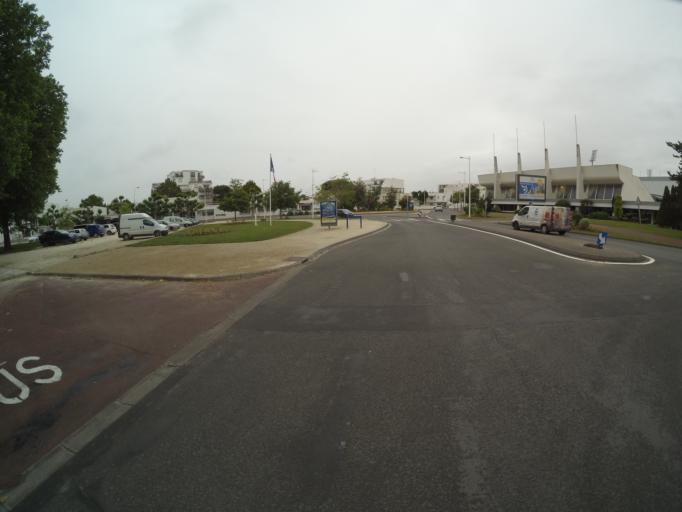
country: FR
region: Poitou-Charentes
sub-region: Departement de la Charente-Maritime
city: Royan
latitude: 45.6260
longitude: -1.0190
